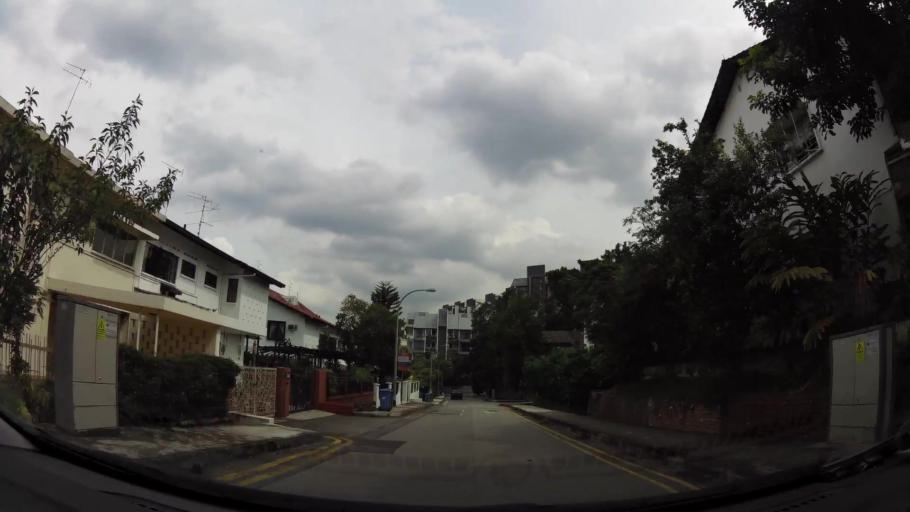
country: SG
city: Singapore
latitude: 1.3121
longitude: 103.7986
